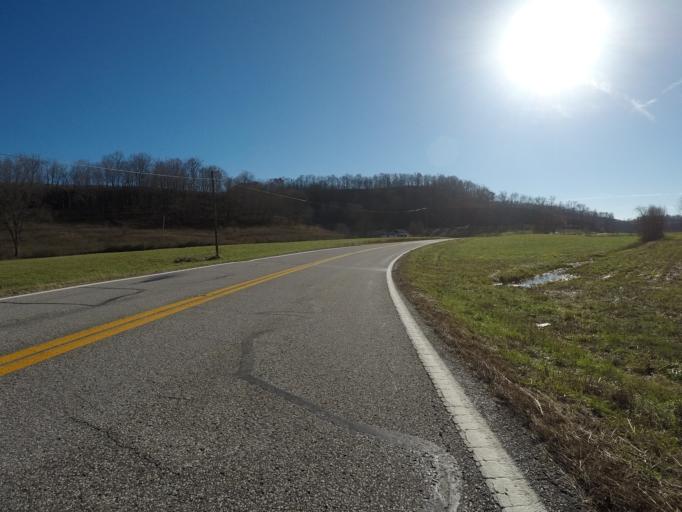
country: US
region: West Virginia
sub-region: Cabell County
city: Huntington
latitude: 38.4845
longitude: -82.4482
